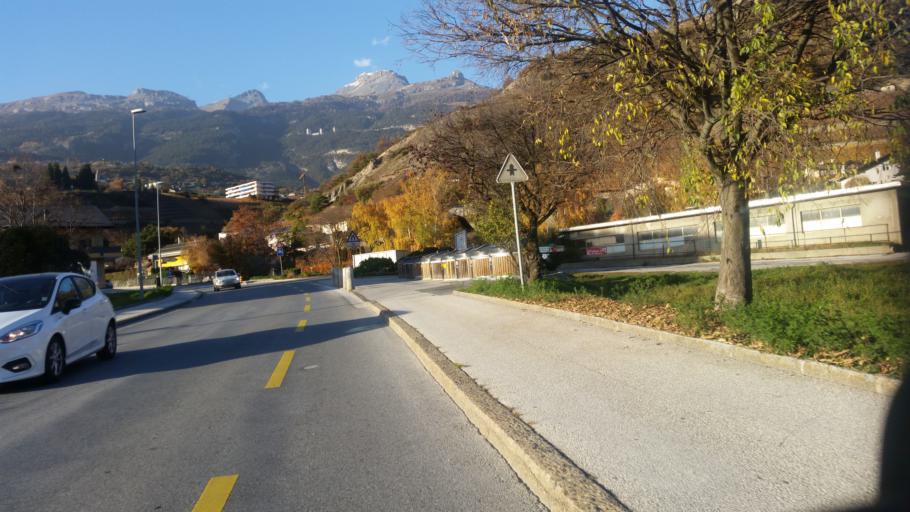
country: CH
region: Valais
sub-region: Sierre District
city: Veyras
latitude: 46.2975
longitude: 7.5444
